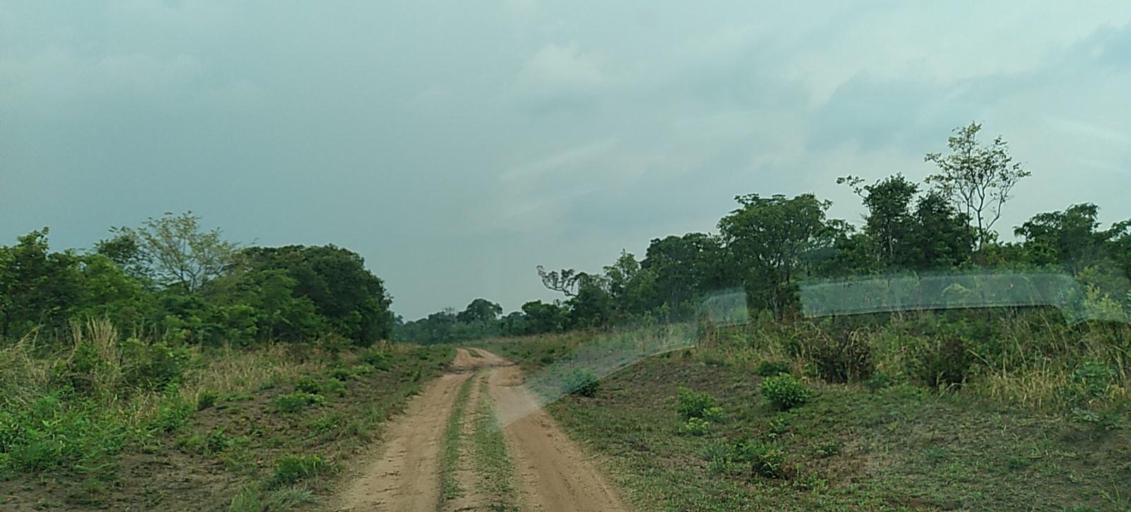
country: ZM
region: North-Western
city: Mwinilunga
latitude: -11.4423
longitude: 24.5927
